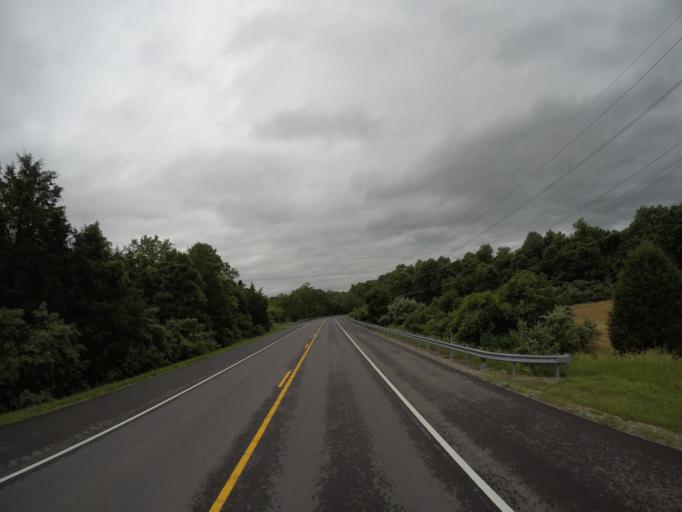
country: US
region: Maryland
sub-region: Washington County
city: Keedysville
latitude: 39.4688
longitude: -77.7162
